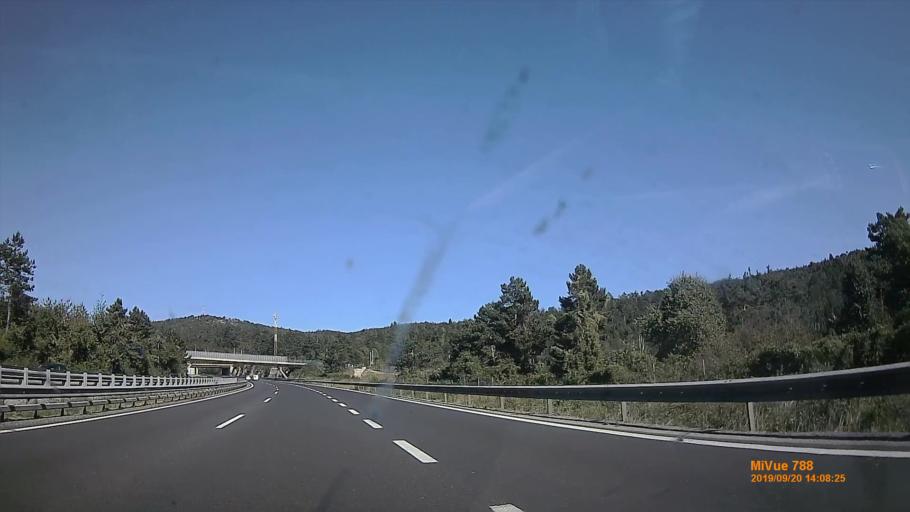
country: SI
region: Postojna
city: Postojna
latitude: 45.7668
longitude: 14.2190
